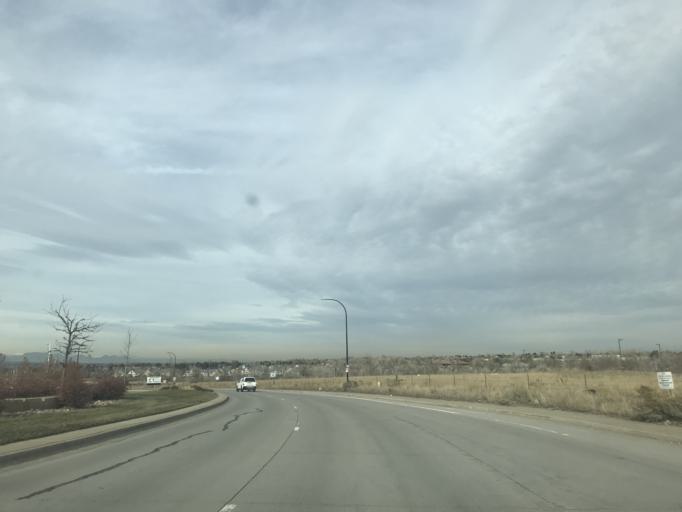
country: US
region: Colorado
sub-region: Douglas County
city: Highlands Ranch
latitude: 39.5613
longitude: -105.0077
